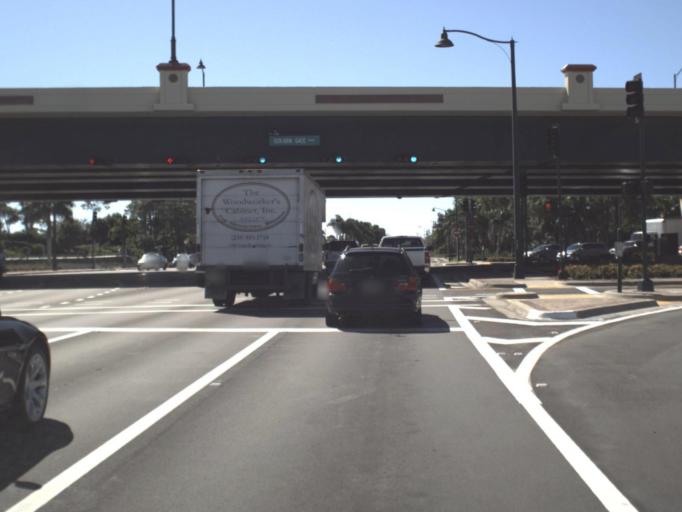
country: US
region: Florida
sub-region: Collier County
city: Naples
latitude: 26.1747
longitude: -81.7671
